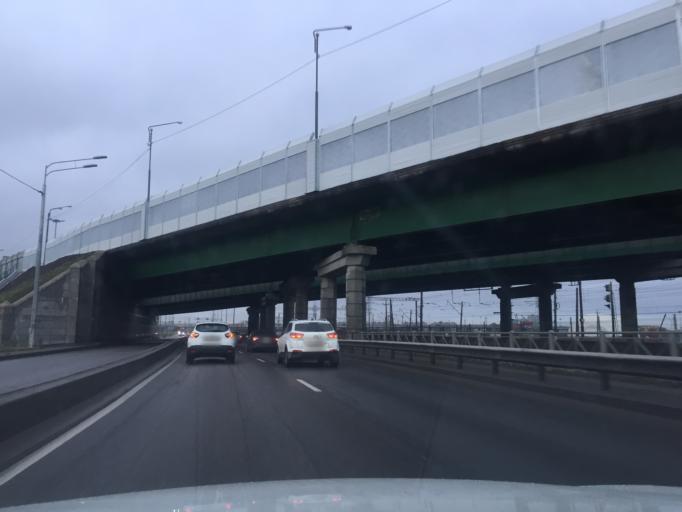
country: RU
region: St.-Petersburg
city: Shushary
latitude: 59.8077
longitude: 30.3867
